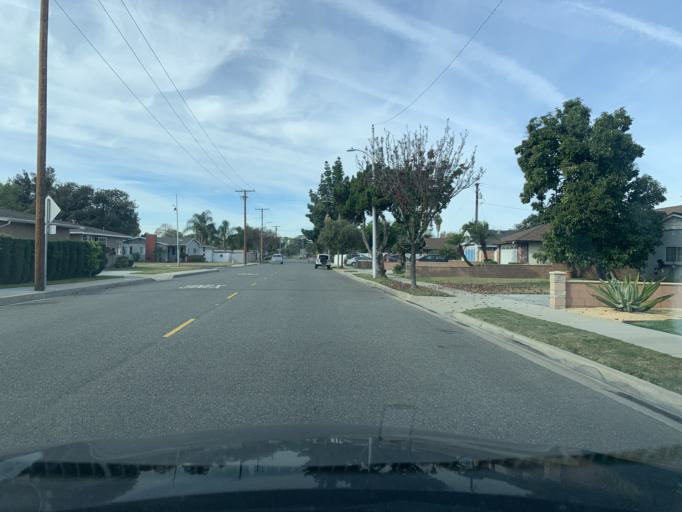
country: US
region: California
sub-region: Los Angeles County
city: West Covina
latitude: 34.0791
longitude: -117.9301
